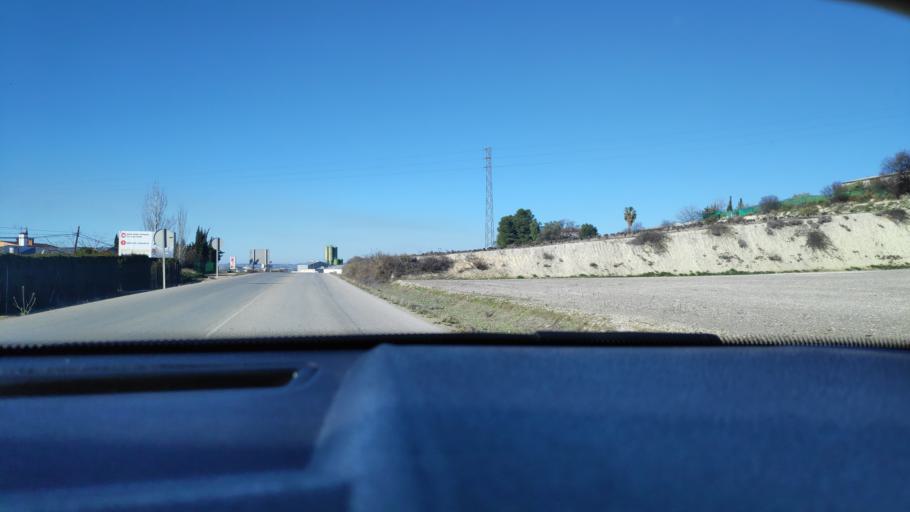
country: ES
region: Andalusia
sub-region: Province of Cordoba
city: Baena
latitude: 37.6230
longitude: -4.3047
